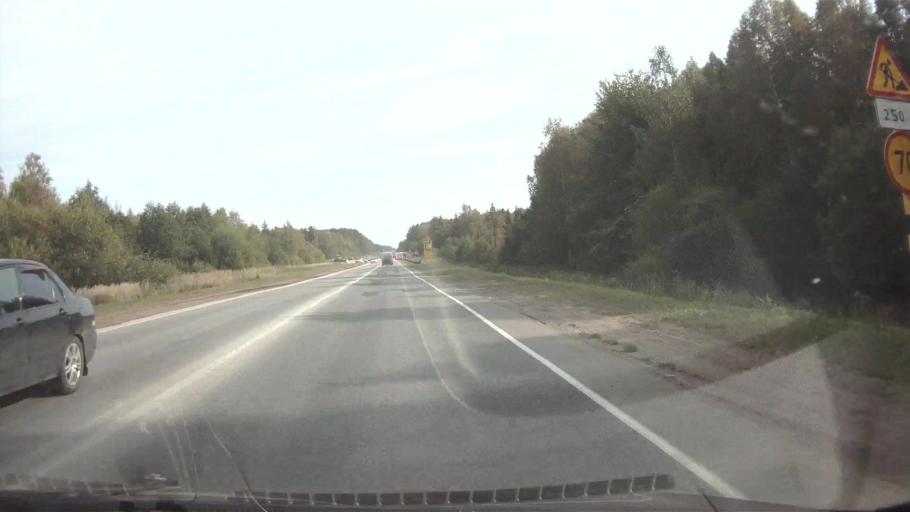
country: RU
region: Mariy-El
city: Sovetskiy
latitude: 56.7406
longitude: 48.4141
